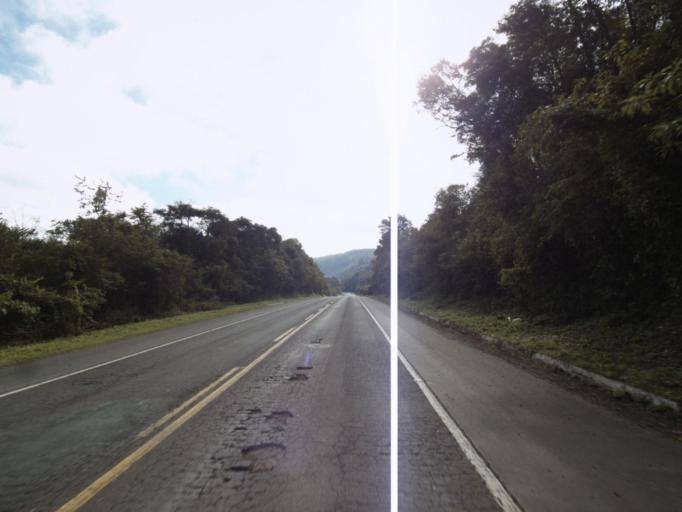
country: BR
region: Rio Grande do Sul
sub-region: Frederico Westphalen
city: Frederico Westphalen
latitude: -27.1499
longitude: -53.2144
